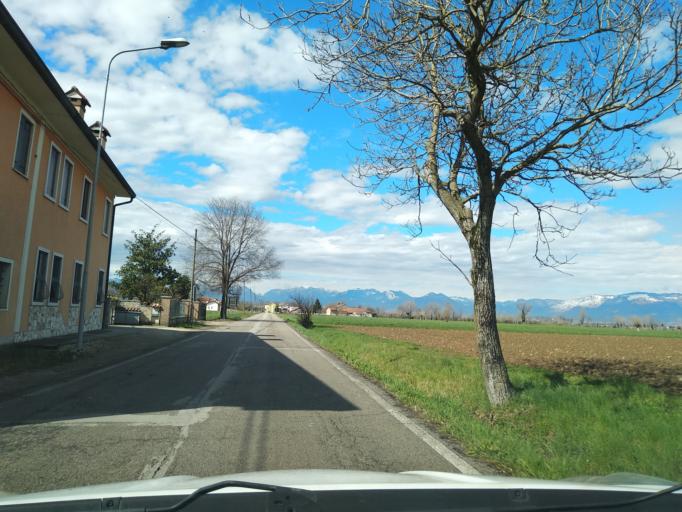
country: IT
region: Veneto
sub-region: Provincia di Vicenza
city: Bolzano Vicentino
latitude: 45.6079
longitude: 11.6091
